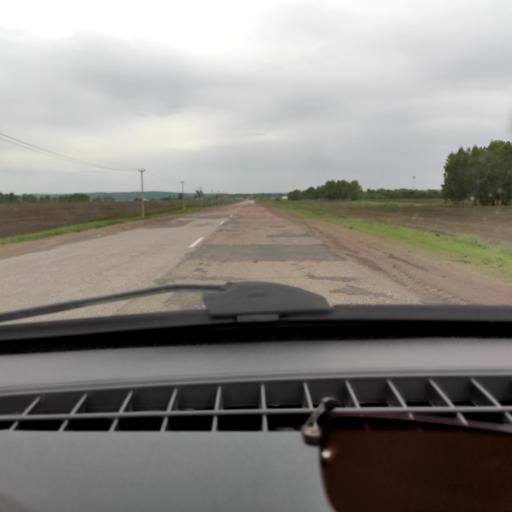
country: RU
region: Bashkortostan
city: Kabakovo
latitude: 54.5426
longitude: 56.0784
